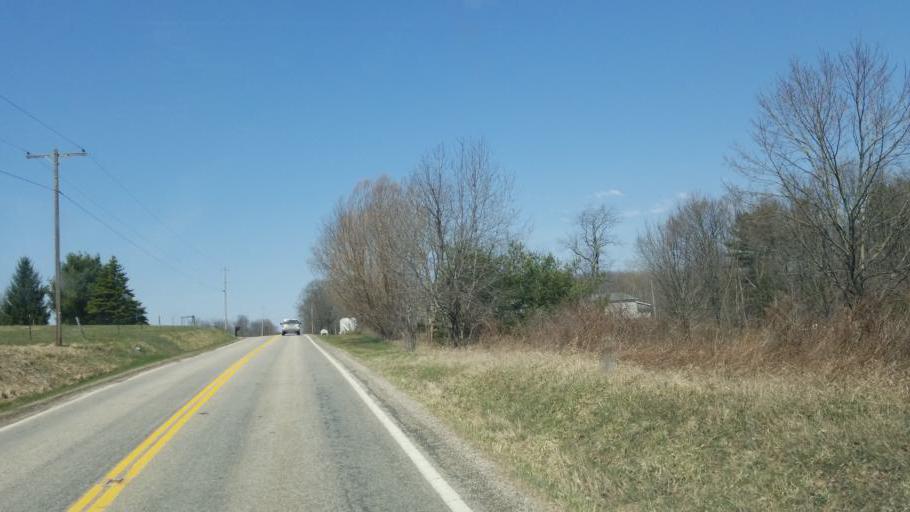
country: US
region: Ohio
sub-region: Ashland County
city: Loudonville
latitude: 40.7374
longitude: -82.1998
